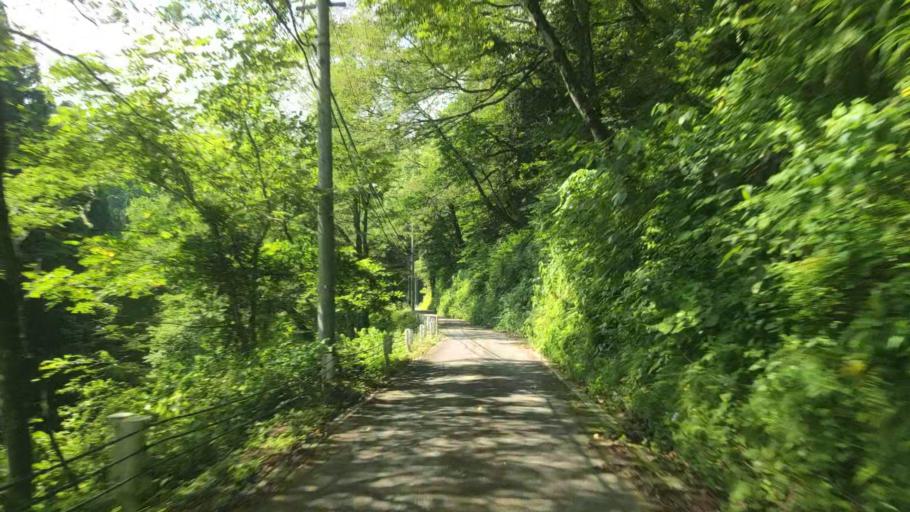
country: JP
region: Ishikawa
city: Komatsu
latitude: 36.2416
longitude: 136.5313
